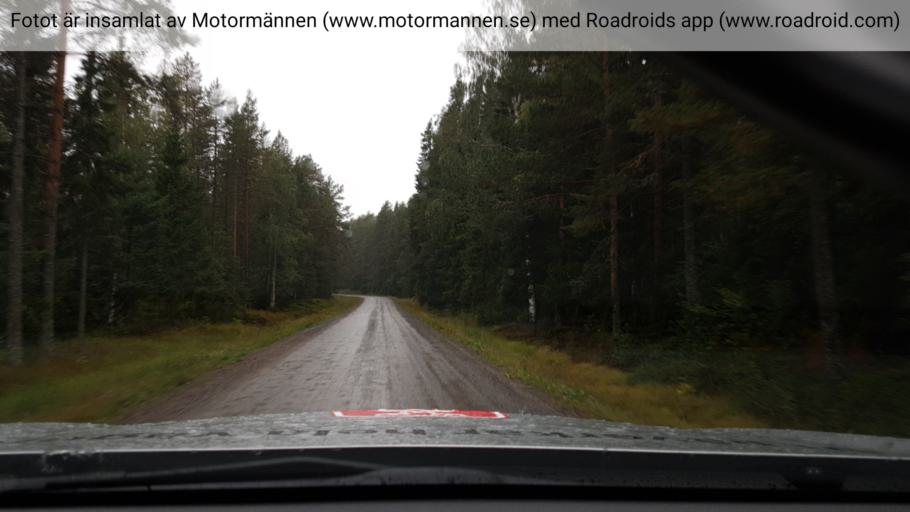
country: SE
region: Vaesterbotten
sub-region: Skelleftea Kommun
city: Burea
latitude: 64.3738
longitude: 21.1920
